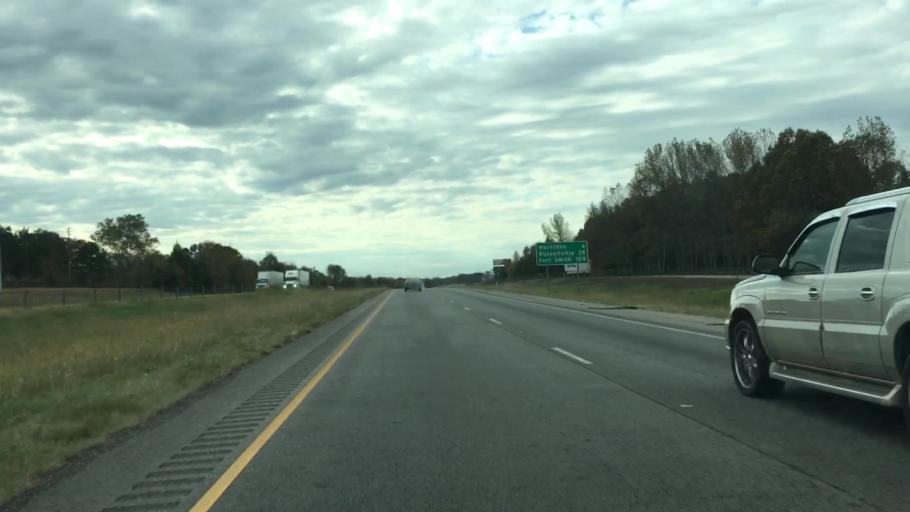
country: US
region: Arkansas
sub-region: Conway County
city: Morrilton
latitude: 35.1628
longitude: -92.6544
